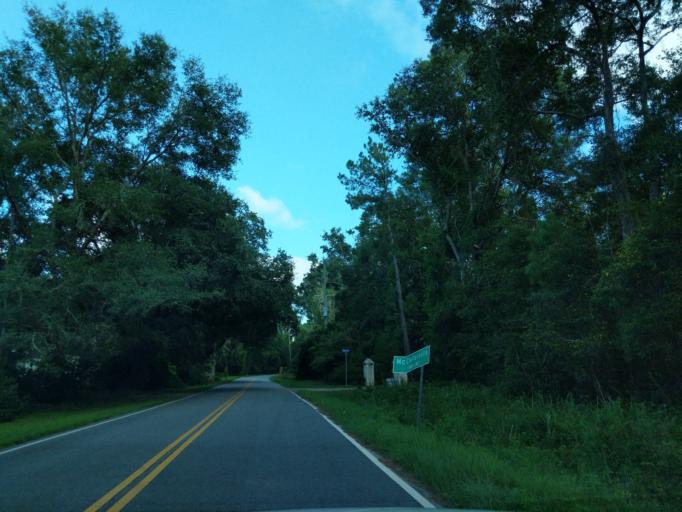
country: US
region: South Carolina
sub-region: Charleston County
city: Awendaw
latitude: 33.0972
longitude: -79.4672
